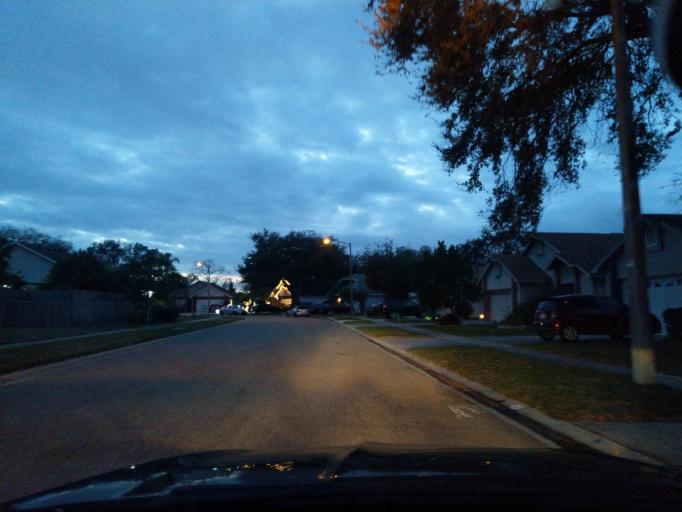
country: US
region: Florida
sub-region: Orange County
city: Williamsburg
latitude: 28.3986
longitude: -81.4197
